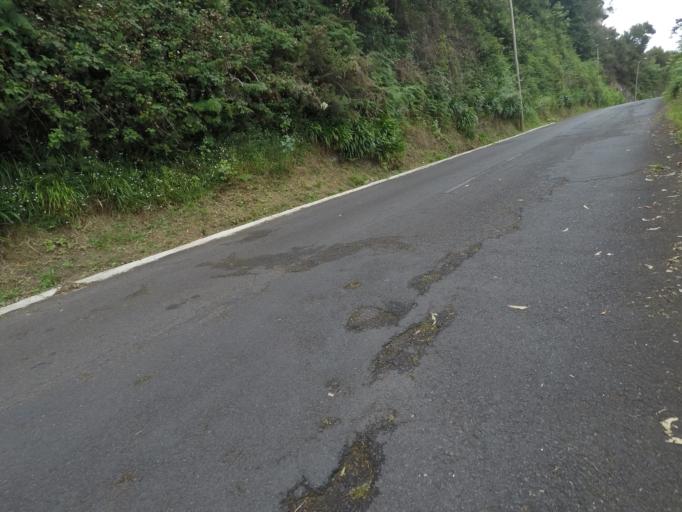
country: PT
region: Madeira
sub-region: Santana
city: Santana
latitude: 32.7952
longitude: -16.8651
